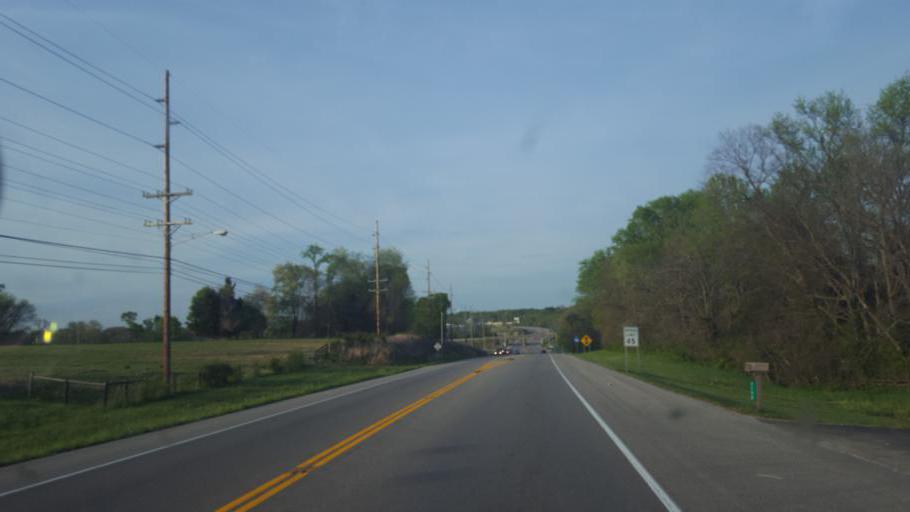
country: US
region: Kentucky
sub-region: Barren County
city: Glasgow
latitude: 36.9739
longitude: -85.9388
